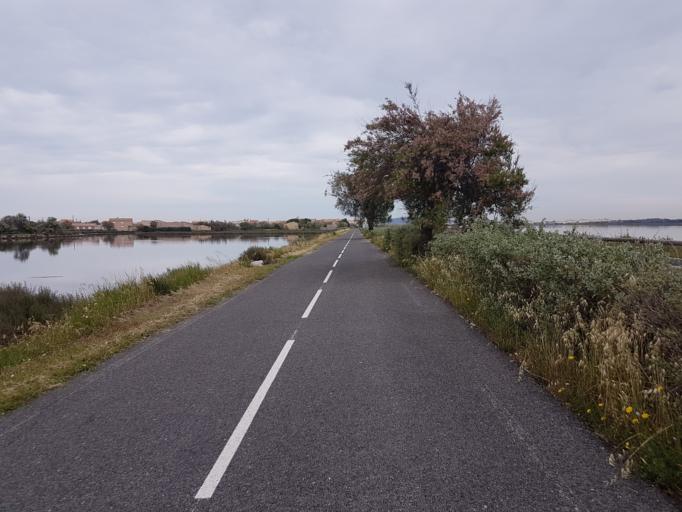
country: FR
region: Languedoc-Roussillon
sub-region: Departement de l'Herault
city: Frontignan
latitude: 43.4394
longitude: 3.7864
